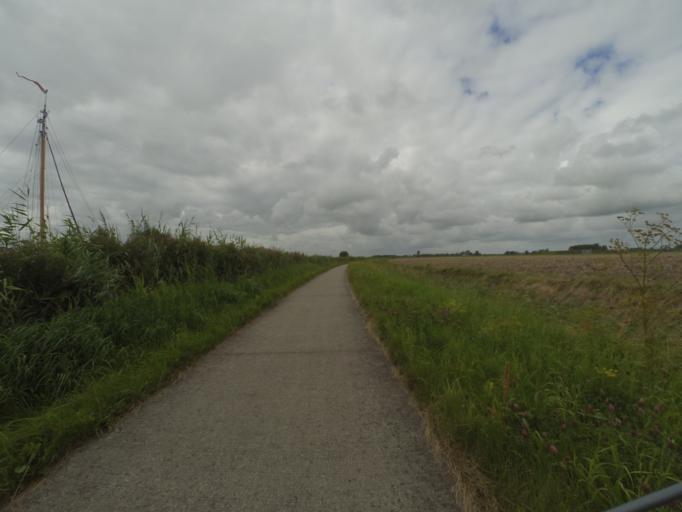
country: NL
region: Friesland
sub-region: Gemeente Kollumerland en Nieuwkruisland
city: Kollum
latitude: 53.3178
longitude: 6.1275
